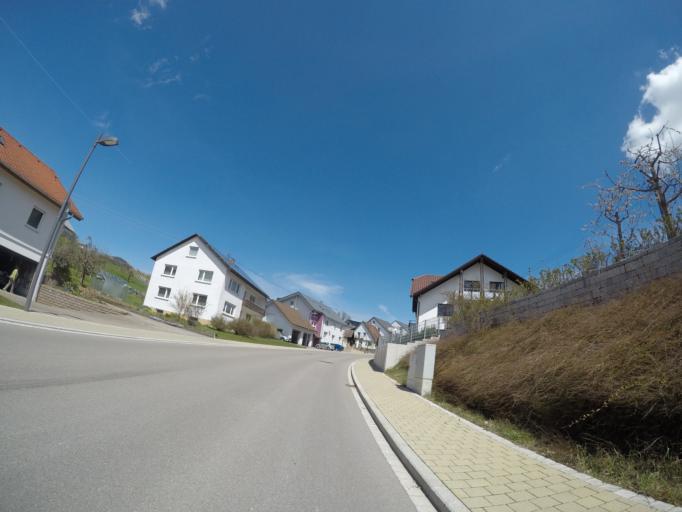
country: DE
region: Baden-Wuerttemberg
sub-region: Tuebingen Region
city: Westerheim
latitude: 48.5130
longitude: 9.6203
